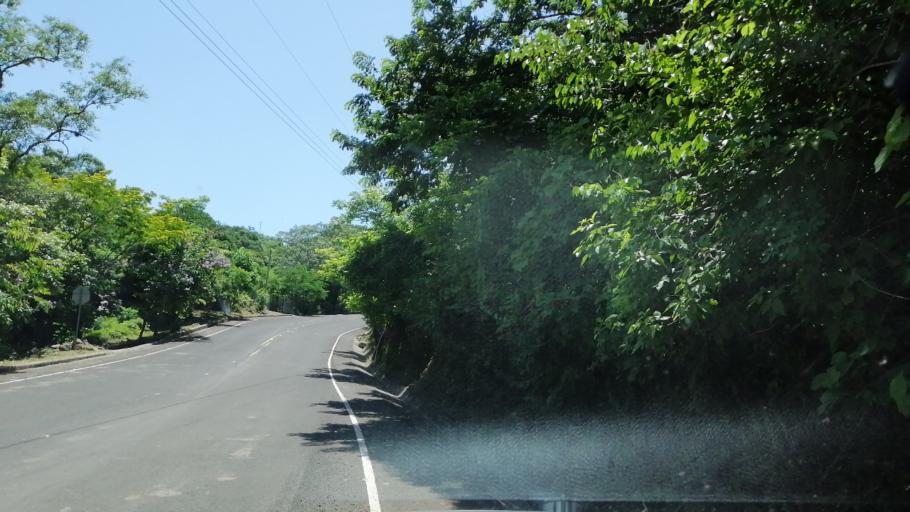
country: SV
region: San Miguel
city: Sesori
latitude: 13.8048
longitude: -88.3824
